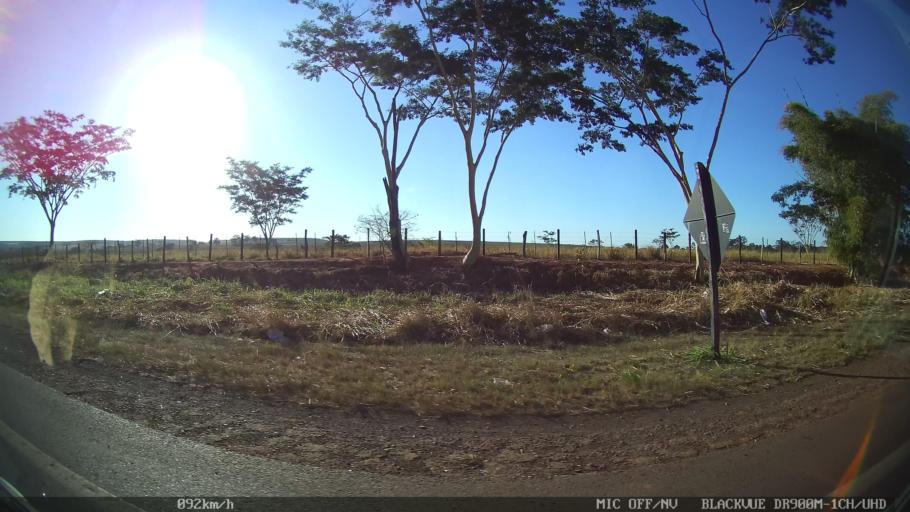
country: BR
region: Sao Paulo
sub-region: Guapiacu
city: Guapiacu
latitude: -20.7675
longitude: -49.2038
